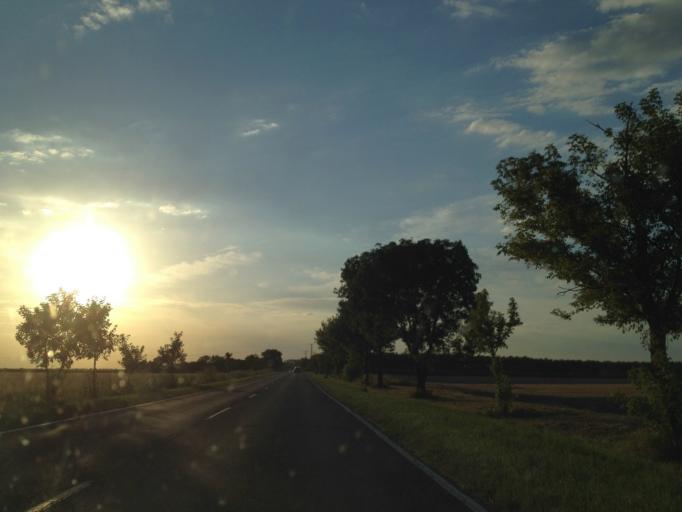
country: HU
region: Gyor-Moson-Sopron
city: Kimle
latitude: 47.8046
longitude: 17.3719
